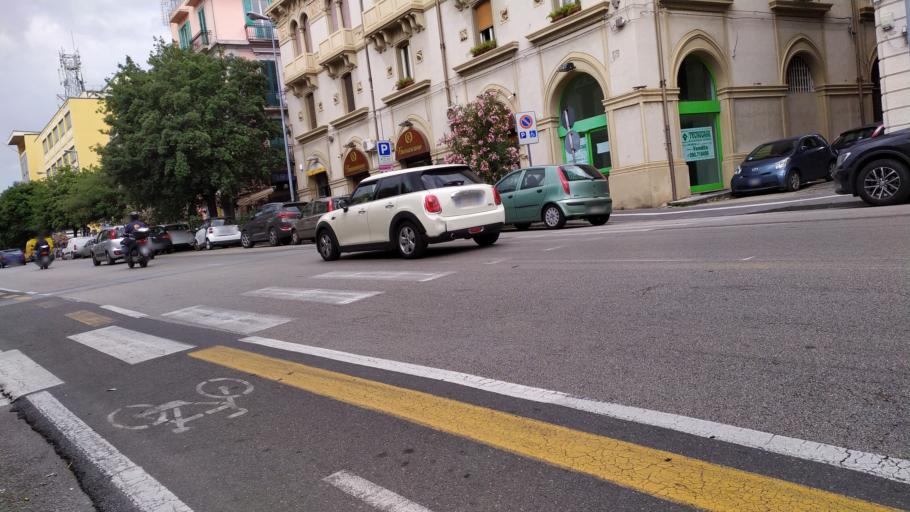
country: IT
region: Sicily
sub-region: Messina
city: Messina
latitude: 38.1911
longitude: 15.5527
